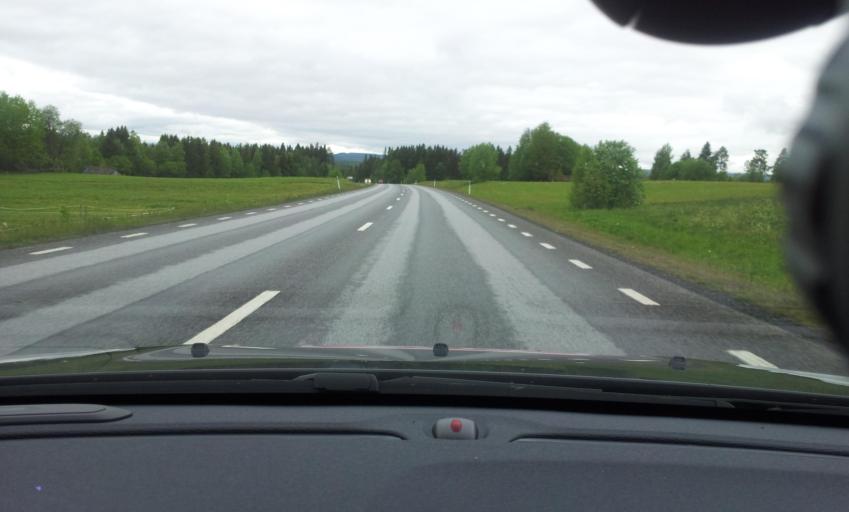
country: SE
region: Jaemtland
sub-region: Krokoms Kommun
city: Valla
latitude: 63.3060
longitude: 13.8722
